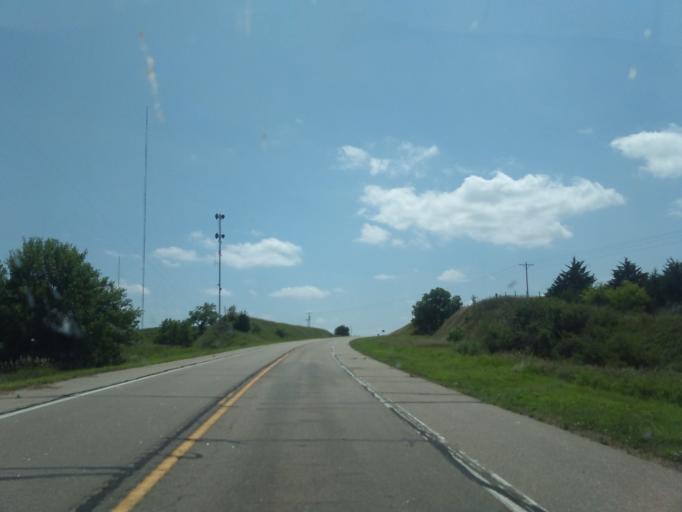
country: US
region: Nebraska
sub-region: Dawson County
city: Lexington
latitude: 40.7031
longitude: -99.7880
